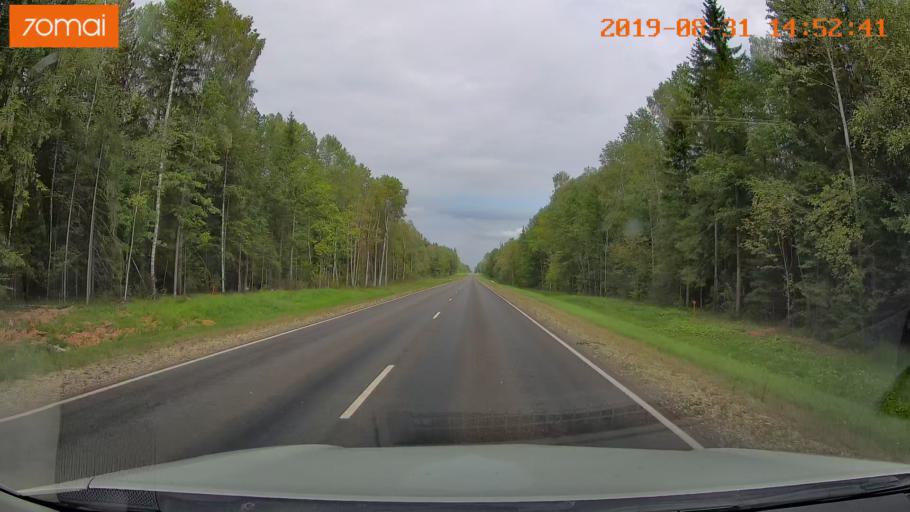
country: RU
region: Kaluga
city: Spas-Demensk
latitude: 54.2778
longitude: 33.8457
